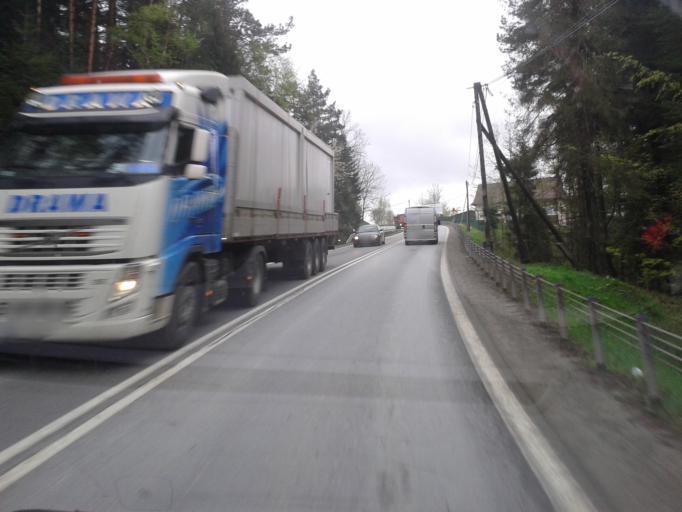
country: PL
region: Lesser Poland Voivodeship
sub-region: Powiat suski
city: Naprawa
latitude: 49.6620
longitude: 19.8913
